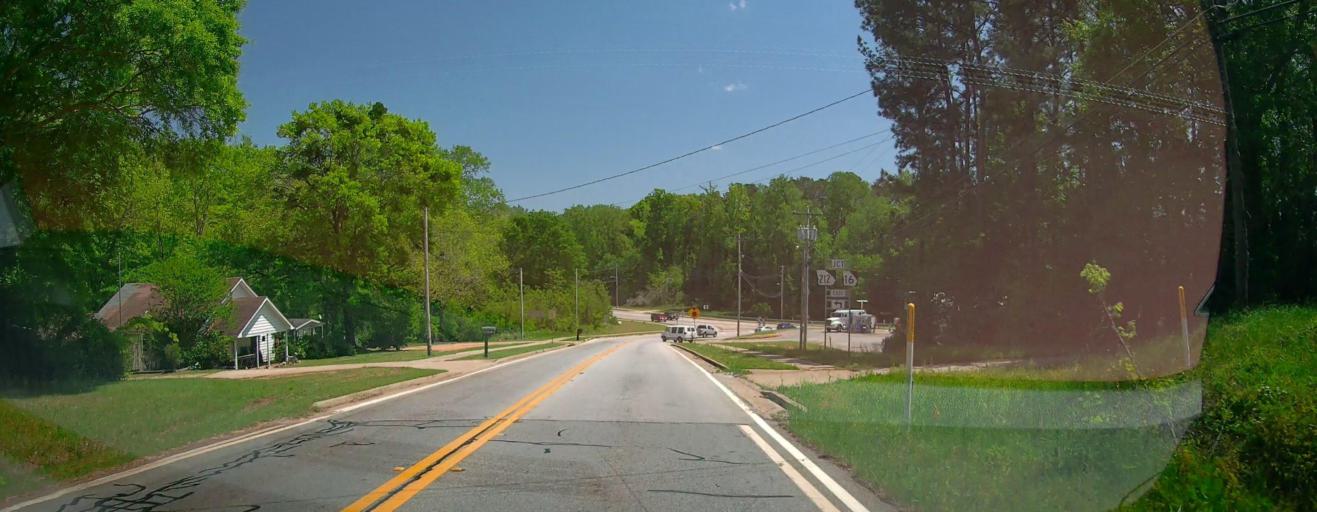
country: US
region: Georgia
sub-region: Jasper County
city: Monticello
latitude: 33.3066
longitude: -83.6964
